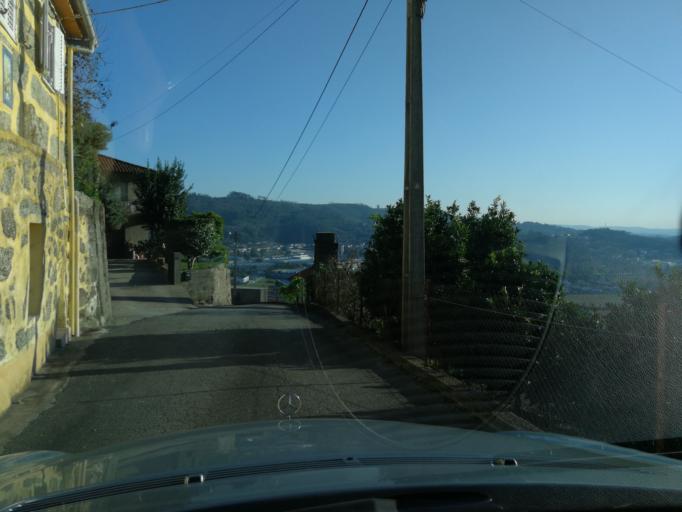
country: PT
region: Braga
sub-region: Braga
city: Oliveira
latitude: 41.4548
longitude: -8.4683
